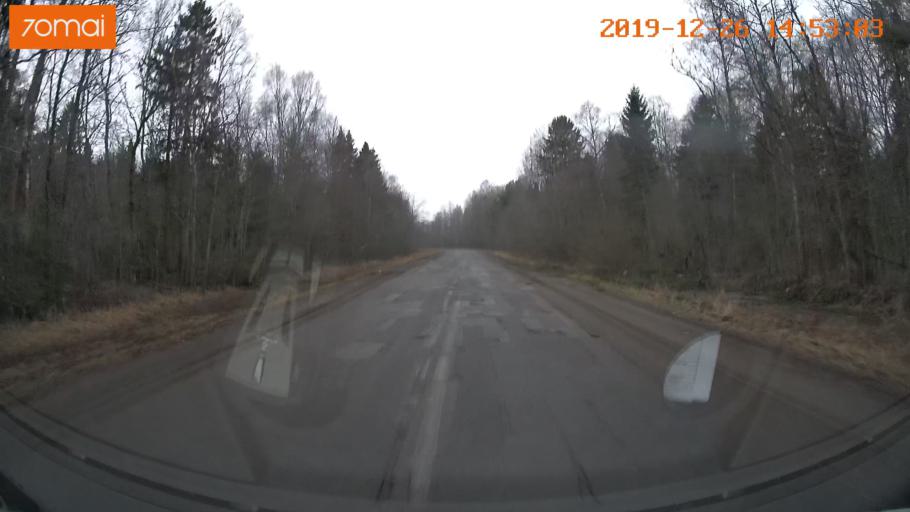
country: RU
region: Jaroslavl
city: Rybinsk
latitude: 58.3178
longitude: 38.8925
